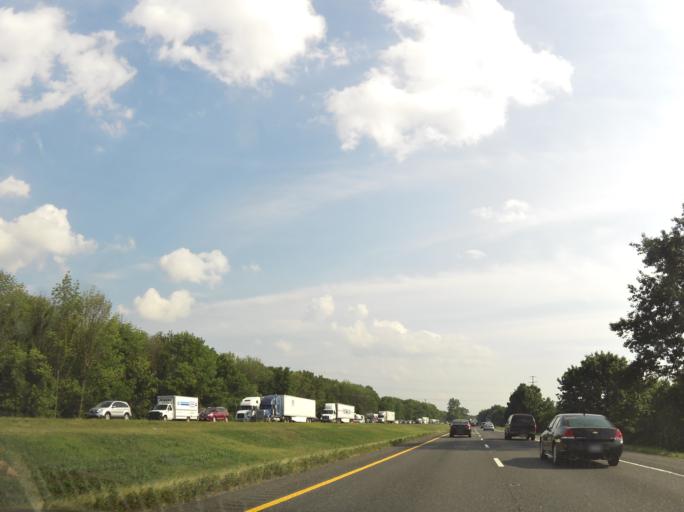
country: US
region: Maryland
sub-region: Washington County
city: Maugansville
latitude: 39.6836
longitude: -77.7335
